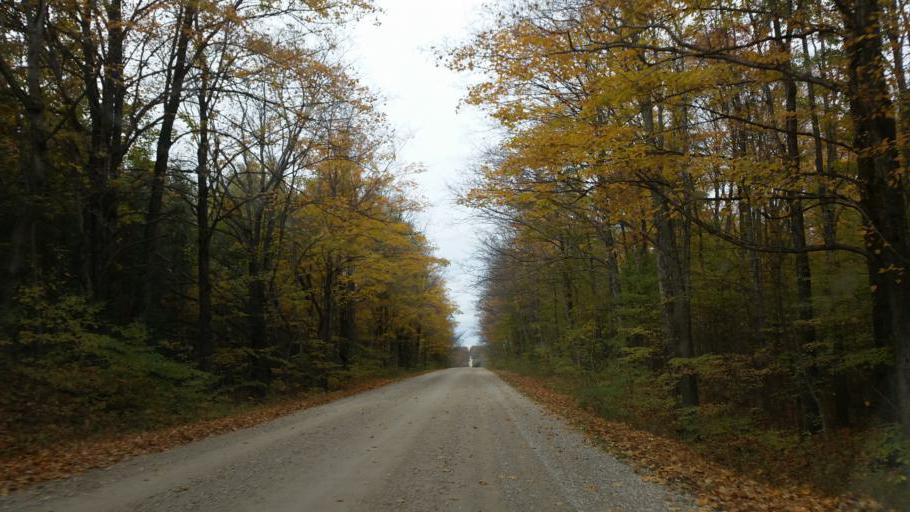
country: CA
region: Ontario
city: Wingham
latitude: 43.9862
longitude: -81.3350
